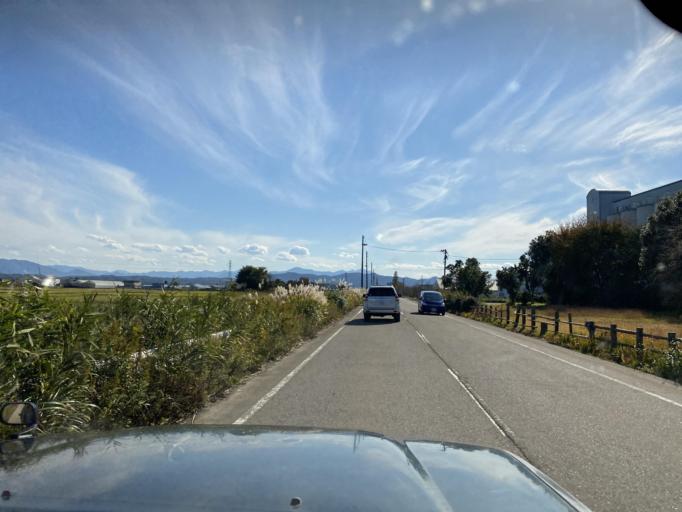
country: JP
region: Niigata
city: Niitsu-honcho
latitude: 37.7959
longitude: 139.0781
